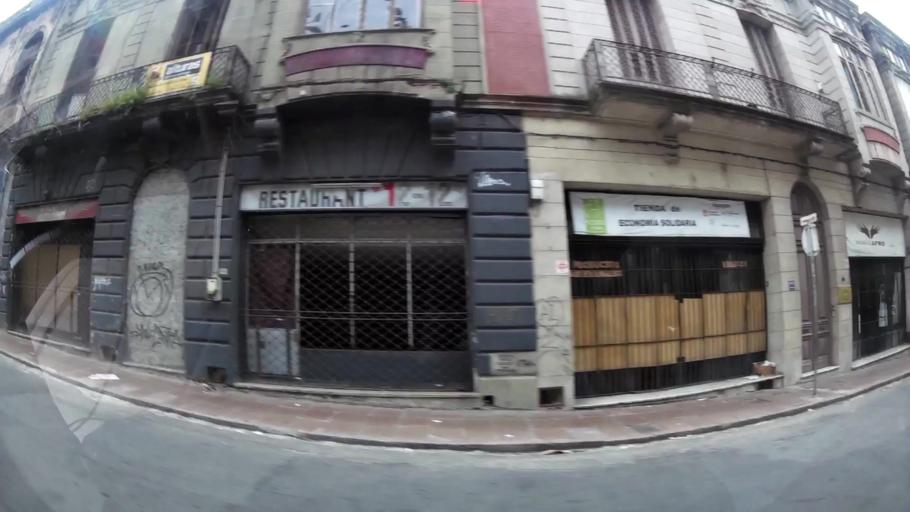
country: UY
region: Montevideo
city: Montevideo
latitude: -34.9045
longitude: -56.2019
